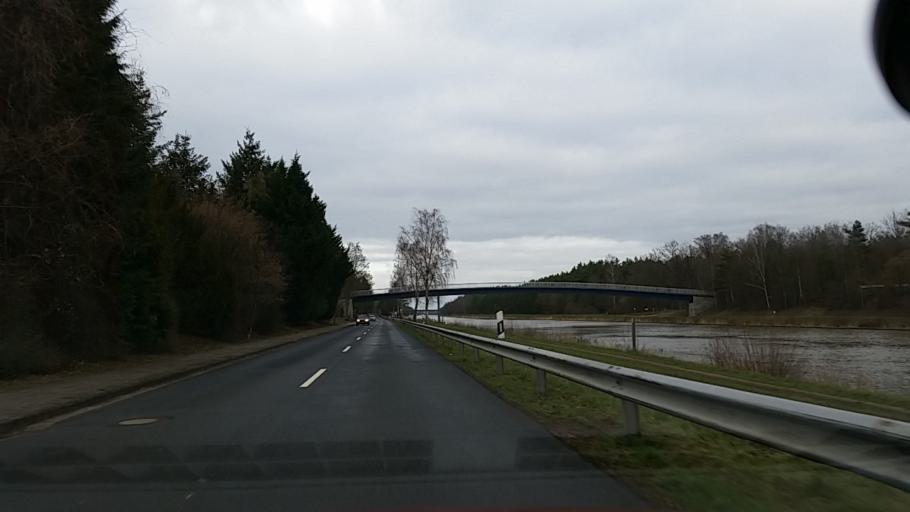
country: DE
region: Lower Saxony
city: Bodenteich
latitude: 52.8380
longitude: 10.6660
